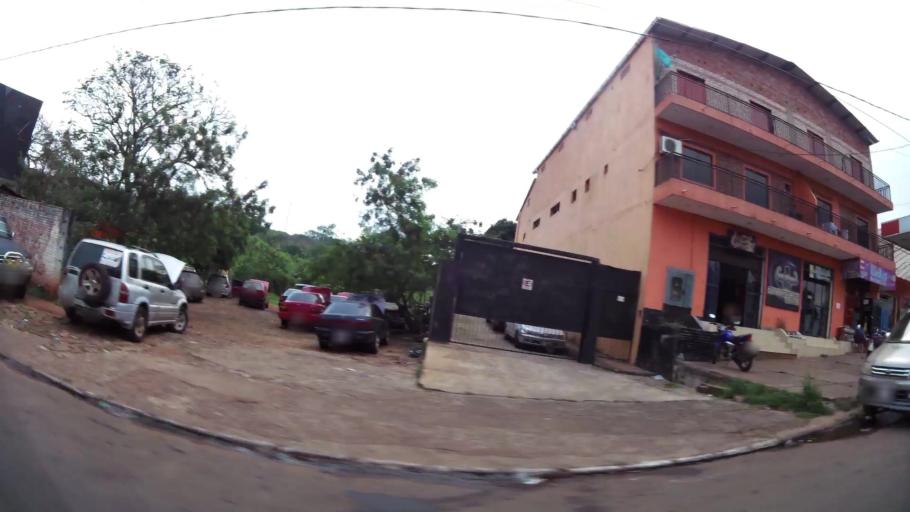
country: PY
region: Alto Parana
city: Presidente Franco
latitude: -25.5471
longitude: -54.6087
